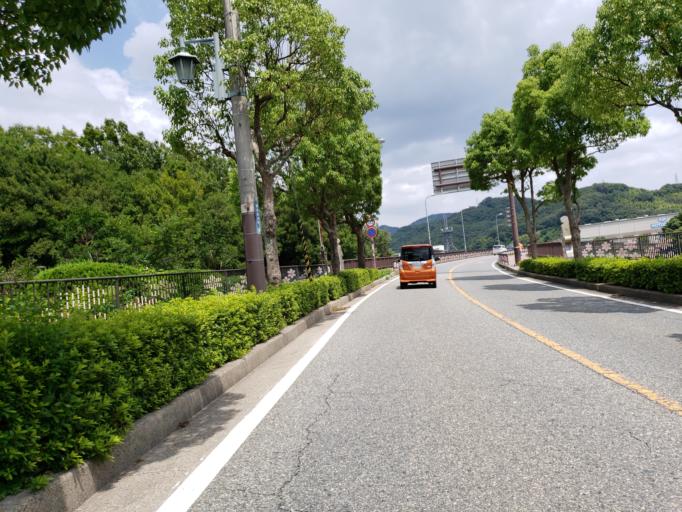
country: JP
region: Hyogo
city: Aioi
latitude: 34.8046
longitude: 134.4633
